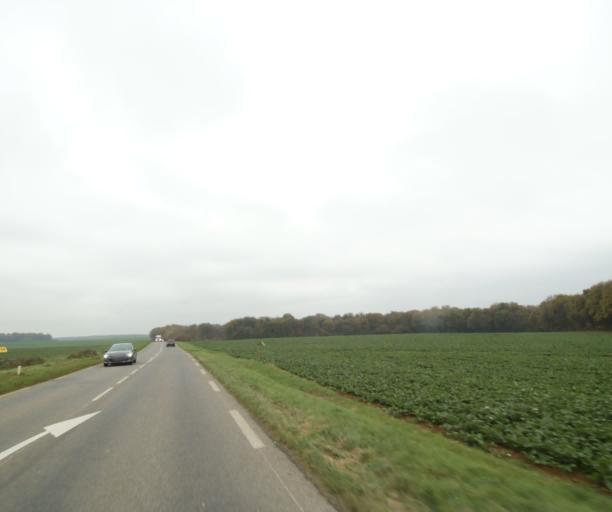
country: FR
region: Lorraine
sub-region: Departement de Meurthe-et-Moselle
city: Moutiers
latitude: 49.2462
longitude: 5.9580
